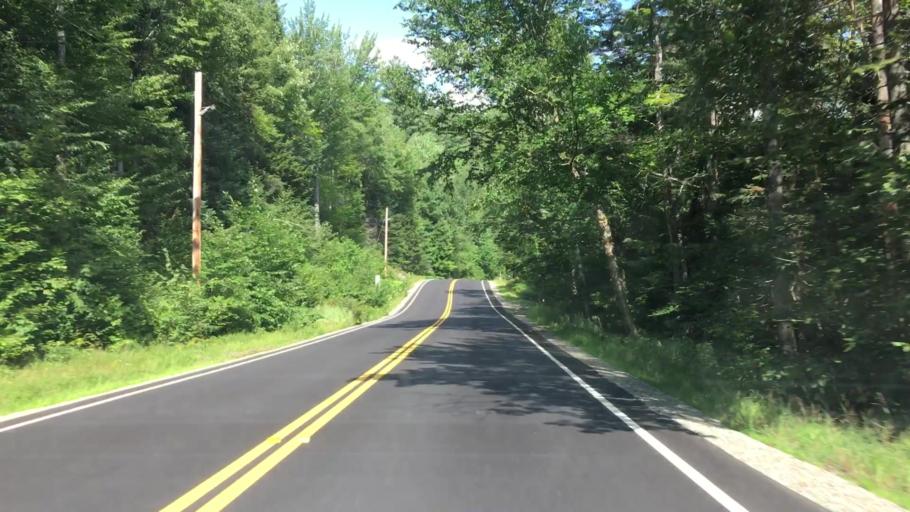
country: US
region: New Hampshire
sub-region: Grafton County
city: North Haverhill
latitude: 44.1056
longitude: -71.8700
